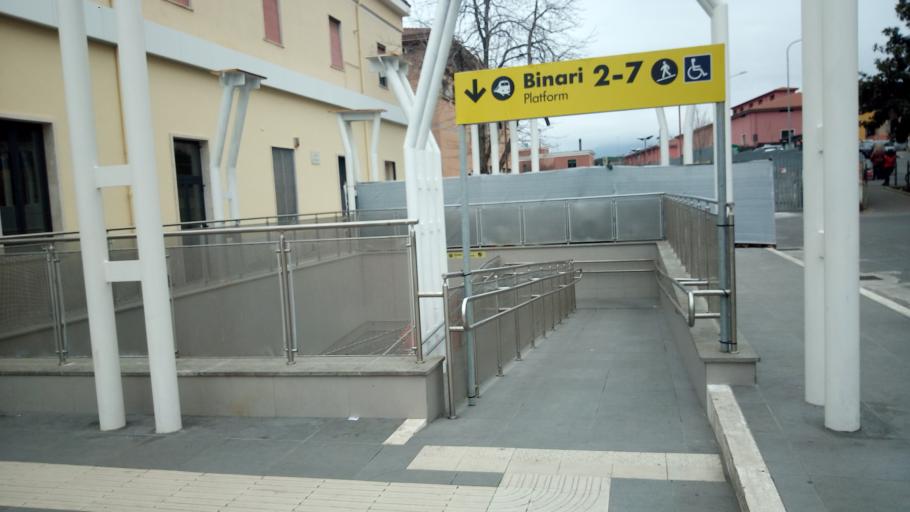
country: IT
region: Latium
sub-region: Citta metropolitana di Roma Capitale
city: Ciampino
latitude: 41.8039
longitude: 12.5993
